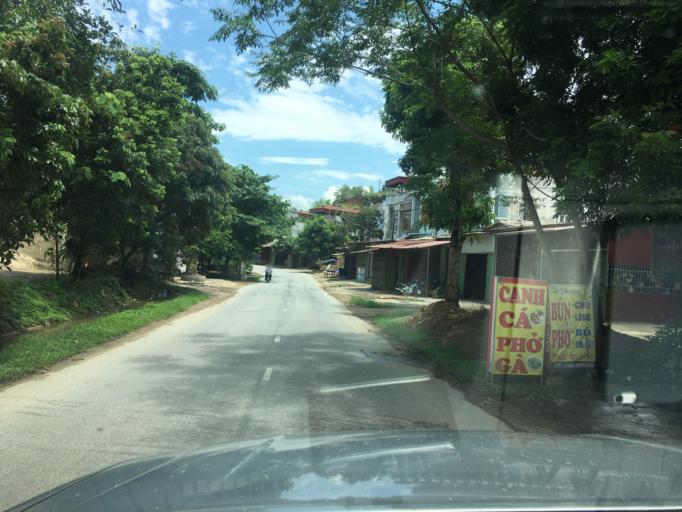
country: VN
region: Yen Bai
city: Son Thinh
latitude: 21.6496
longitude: 104.5005
